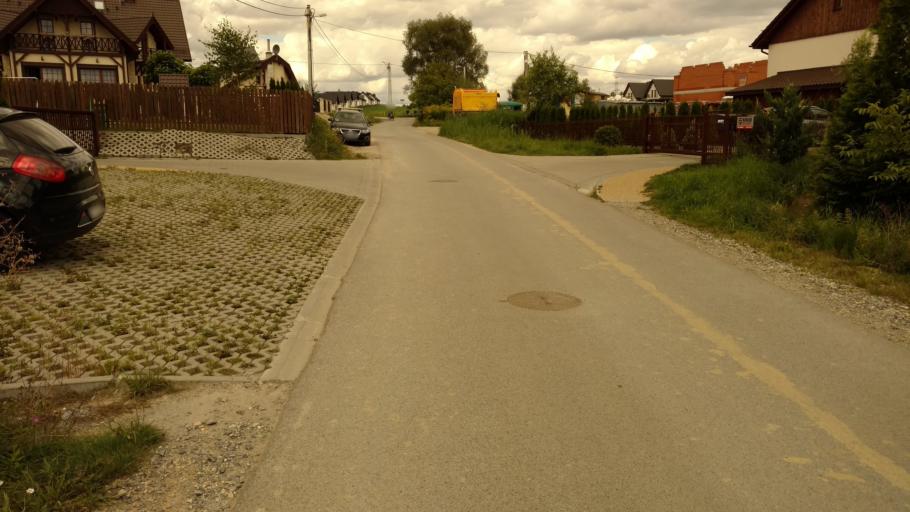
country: PL
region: Lesser Poland Voivodeship
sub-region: Powiat krakowski
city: Michalowice
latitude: 50.1323
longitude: 19.9606
